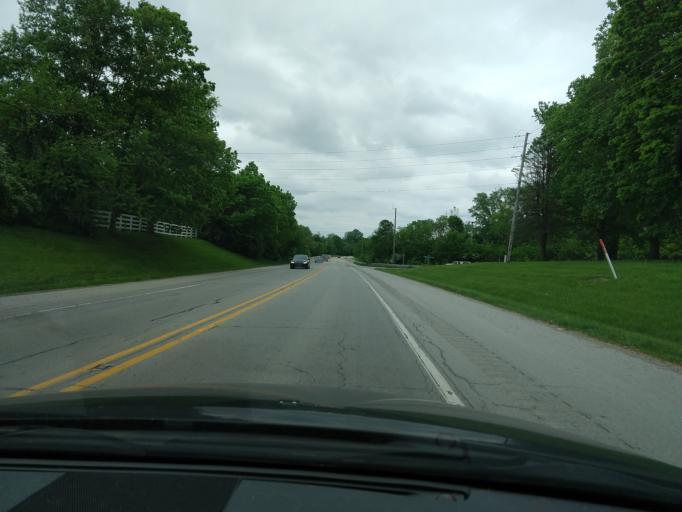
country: US
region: Indiana
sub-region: Hamilton County
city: Noblesville
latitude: 40.0446
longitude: -86.0360
